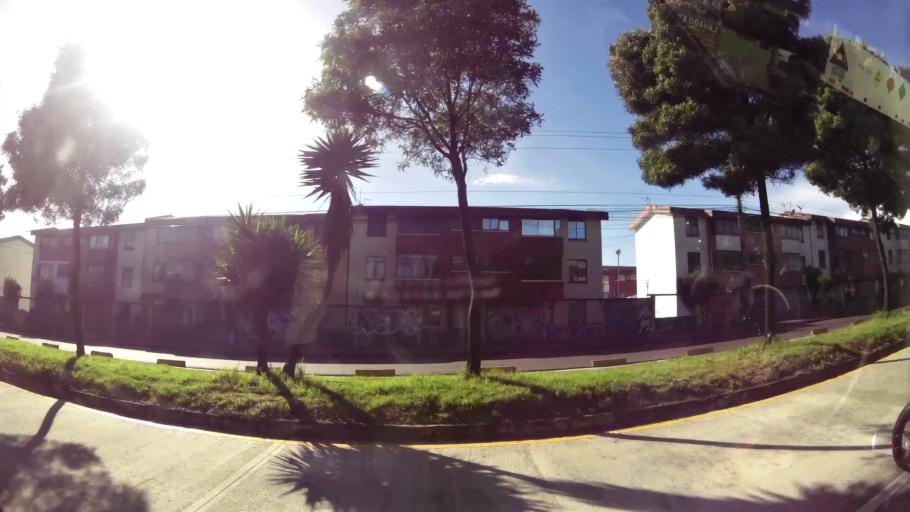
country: EC
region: Pichincha
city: Quito
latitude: -0.3149
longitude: -78.5485
